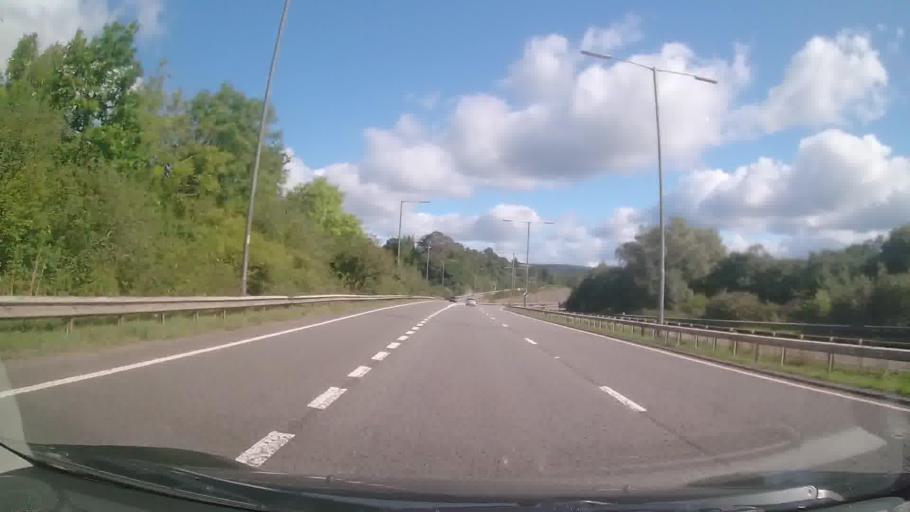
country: GB
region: Wales
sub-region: Neath Port Talbot
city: Neath
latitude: 51.6750
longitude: -3.7863
